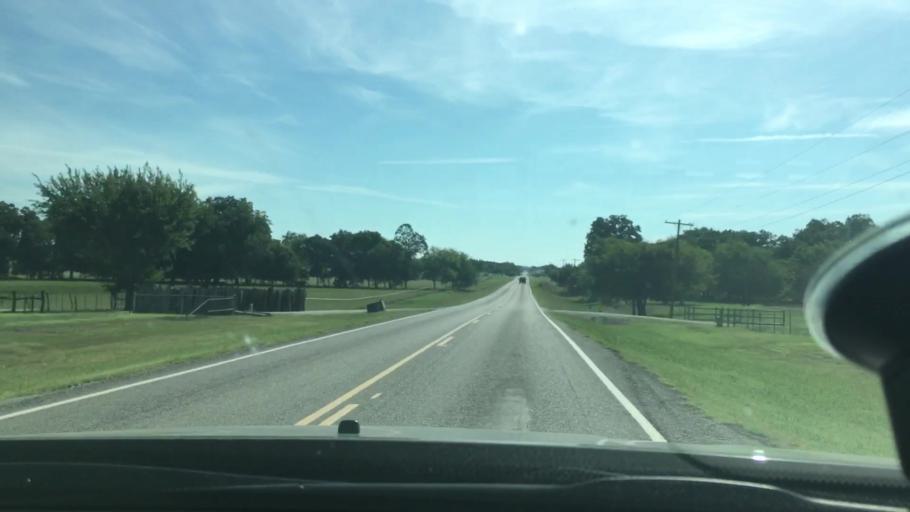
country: US
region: Oklahoma
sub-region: Carter County
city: Ardmore
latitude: 34.3327
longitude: -97.1729
